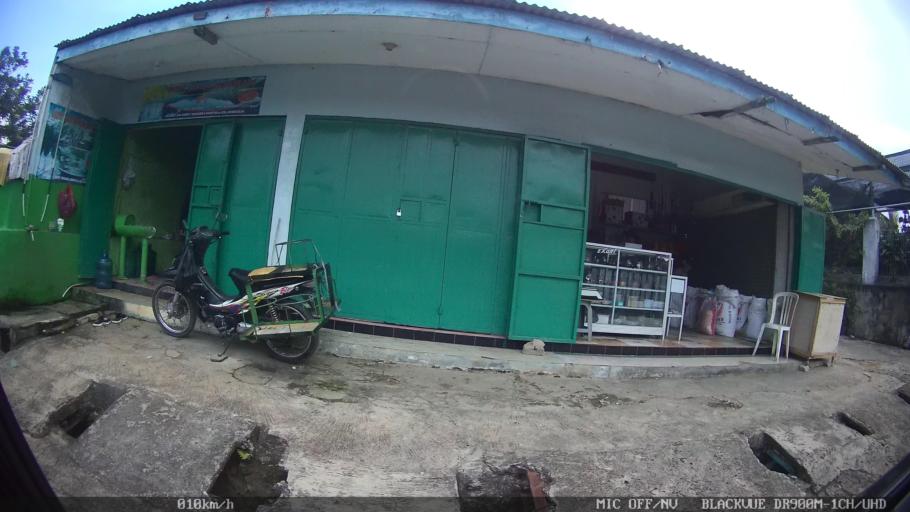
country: ID
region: Lampung
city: Kedaton
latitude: -5.3943
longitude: 105.2118
